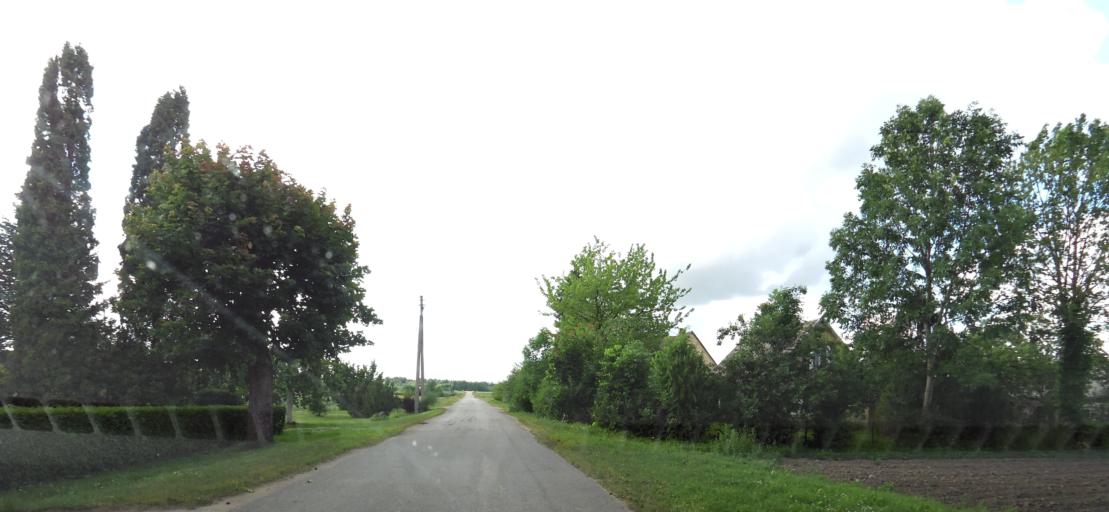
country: LT
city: Obeliai
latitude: 55.8994
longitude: 25.1914
